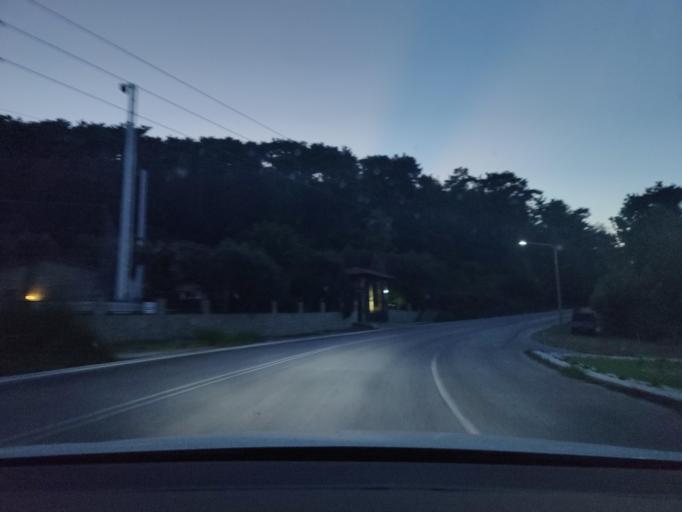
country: GR
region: East Macedonia and Thrace
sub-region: Nomos Kavalas
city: Thasos
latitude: 40.7781
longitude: 24.6841
